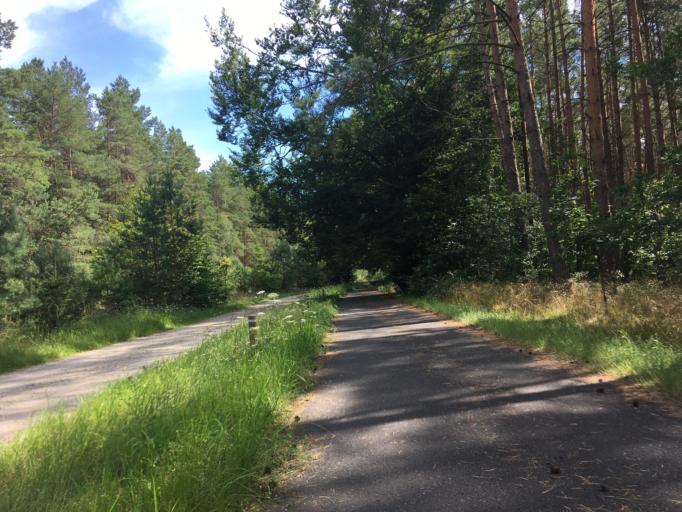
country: DE
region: Brandenburg
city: Rheinsberg
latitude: 53.0754
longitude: 12.9051
